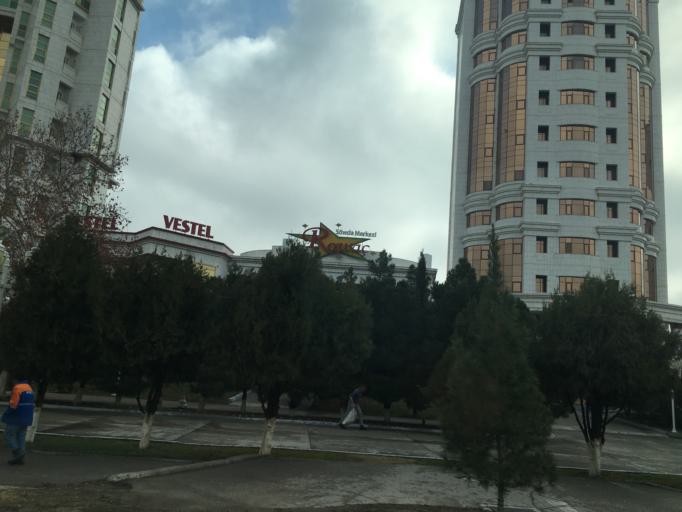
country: TM
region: Ahal
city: Ashgabat
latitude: 37.9223
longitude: 58.3755
